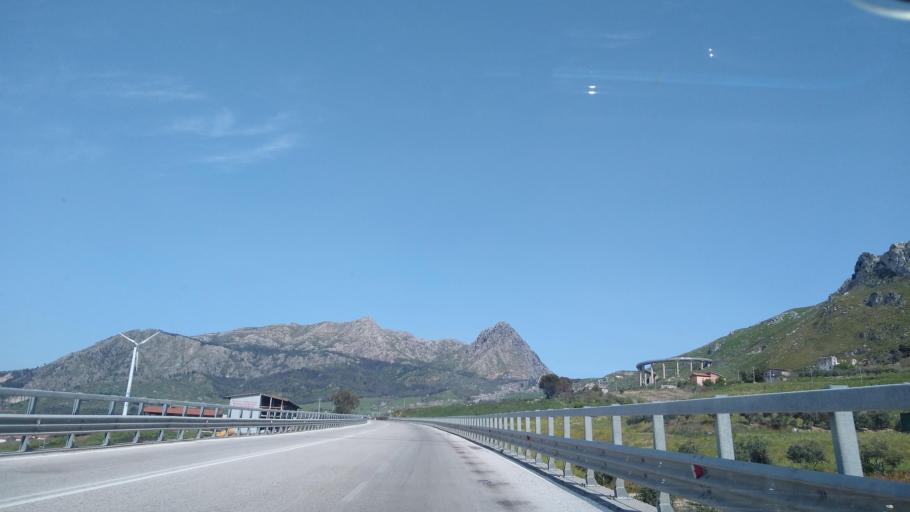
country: IT
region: Sicily
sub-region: Palermo
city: San Giuseppe Jato
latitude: 37.9760
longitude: 13.2152
